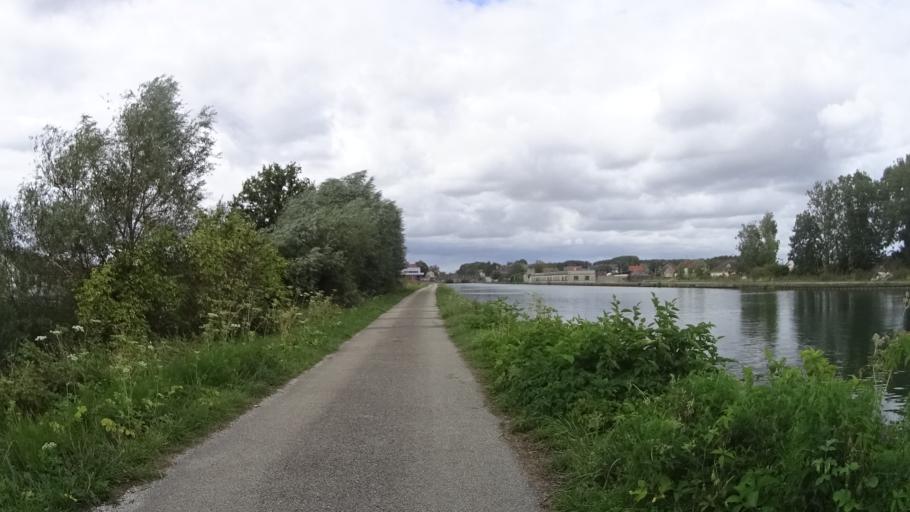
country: FR
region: Picardie
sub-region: Departement de l'Aisne
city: Tergnier
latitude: 49.6525
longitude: 3.3033
